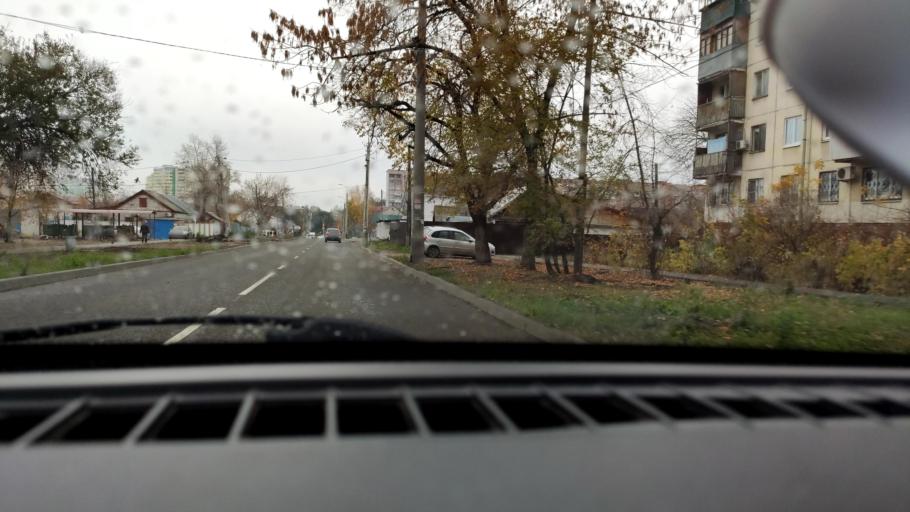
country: RU
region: Samara
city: Samara
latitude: 53.2005
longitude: 50.2037
